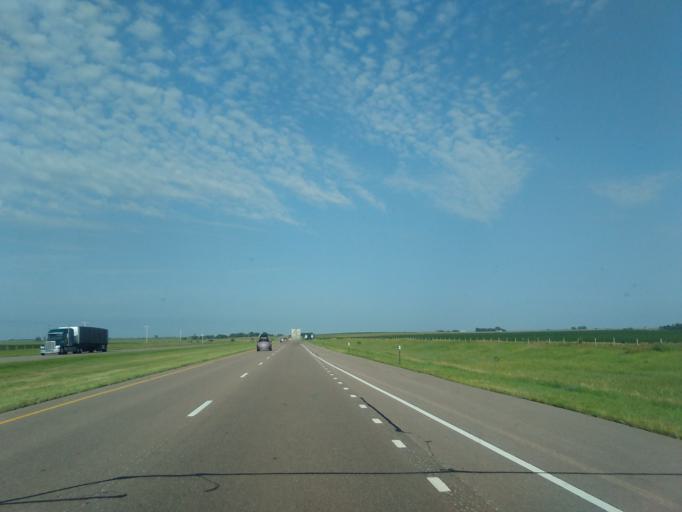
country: US
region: Nebraska
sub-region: York County
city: York
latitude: 40.8213
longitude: -97.6862
